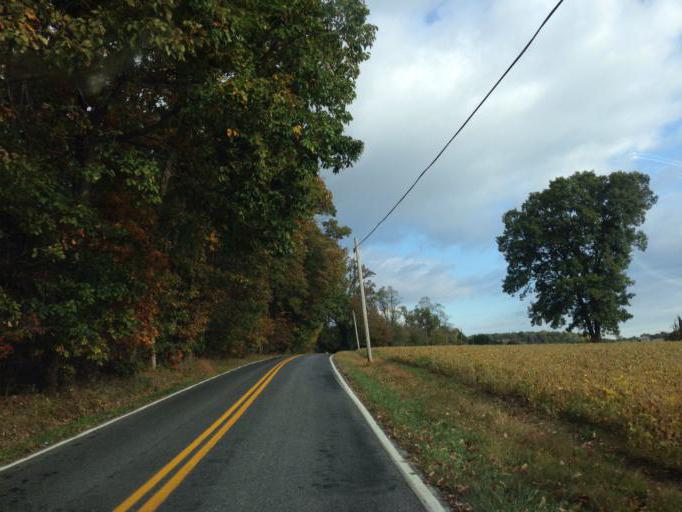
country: US
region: Maryland
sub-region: Carroll County
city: Mount Airy
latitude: 39.3278
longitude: -77.1454
